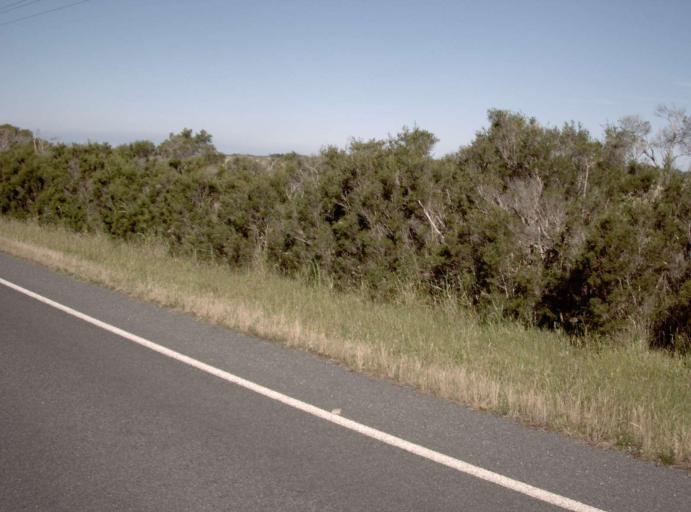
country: AU
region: Victoria
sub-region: Latrobe
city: Traralgon
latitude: -38.6324
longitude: 146.5896
